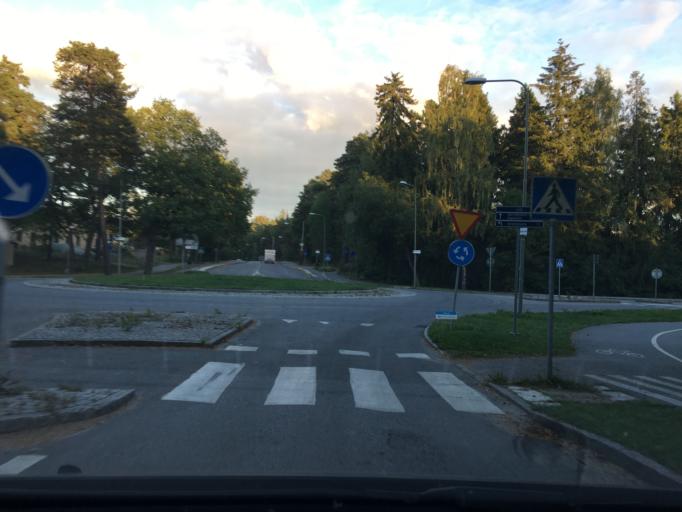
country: SE
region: Stockholm
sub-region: Stockholms Kommun
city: Bromma
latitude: 59.3289
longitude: 17.9544
